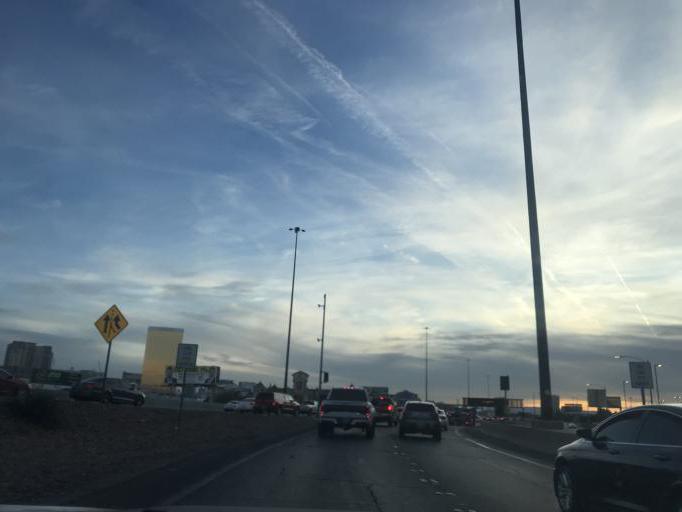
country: US
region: Nevada
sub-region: Clark County
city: Las Vegas
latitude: 36.1431
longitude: -115.1728
